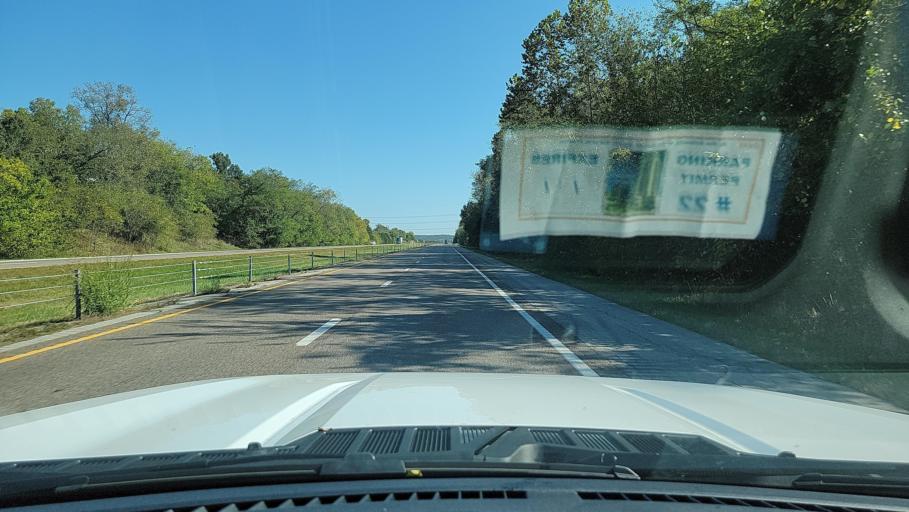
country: US
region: Missouri
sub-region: Jefferson County
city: Crystal City
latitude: 38.1364
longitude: -90.3248
